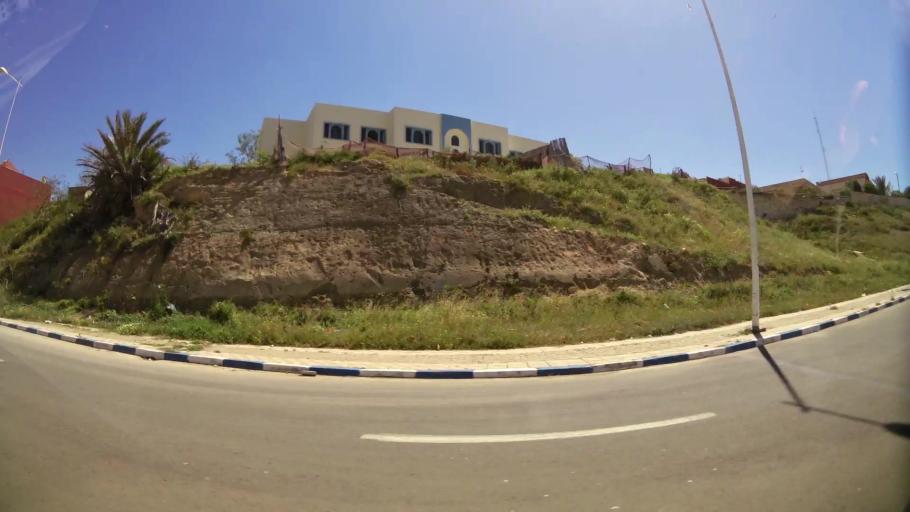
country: MA
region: Oriental
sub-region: Berkane-Taourirt
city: Madagh
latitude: 35.1390
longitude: -2.4228
